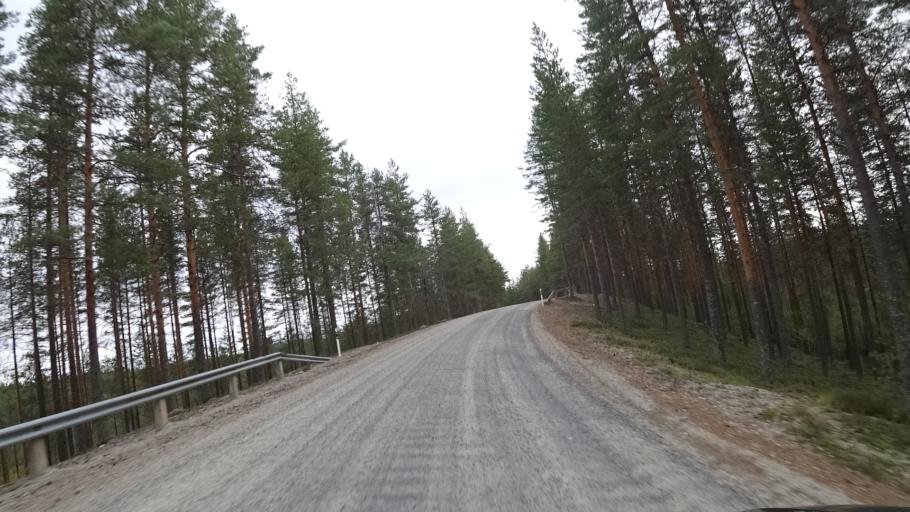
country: FI
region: North Karelia
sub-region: Pielisen Karjala
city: Lieksa
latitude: 63.2588
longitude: 30.3194
